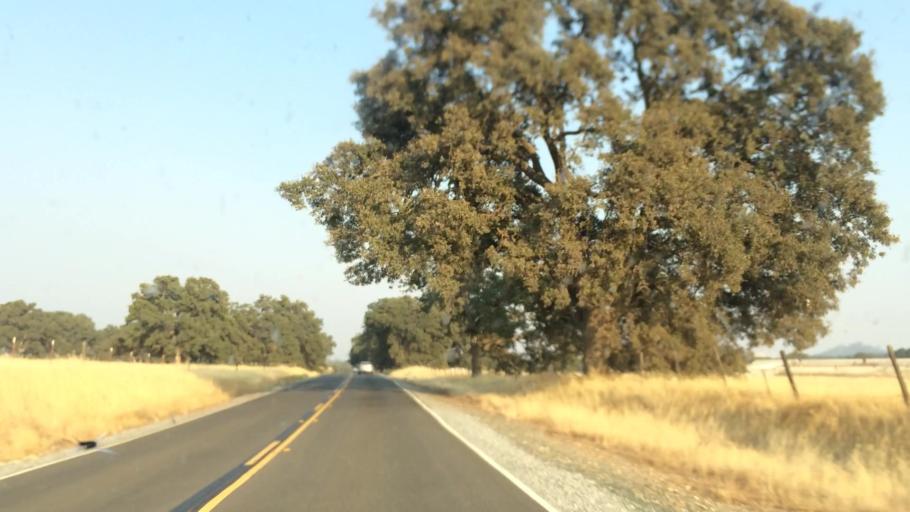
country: US
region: California
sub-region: Amador County
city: Ione
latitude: 38.3995
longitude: -121.0120
